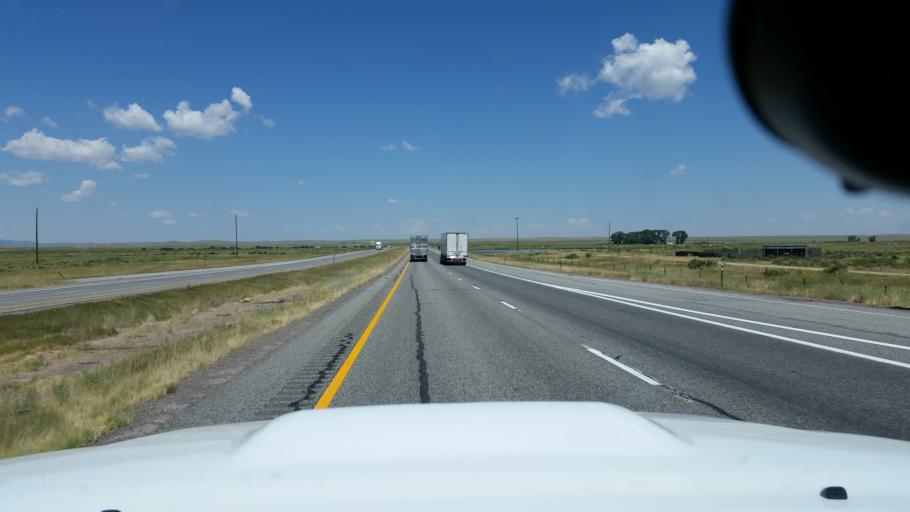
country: US
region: Wyoming
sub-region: Albany County
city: Laramie
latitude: 41.3976
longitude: -105.8263
